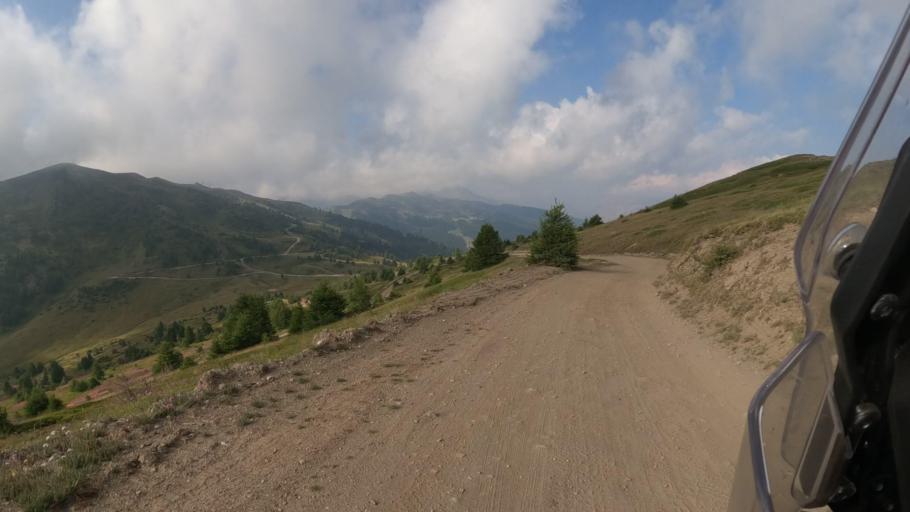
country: IT
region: Piedmont
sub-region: Provincia di Torino
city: Sauze d'Oulx
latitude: 45.0264
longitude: 6.9013
